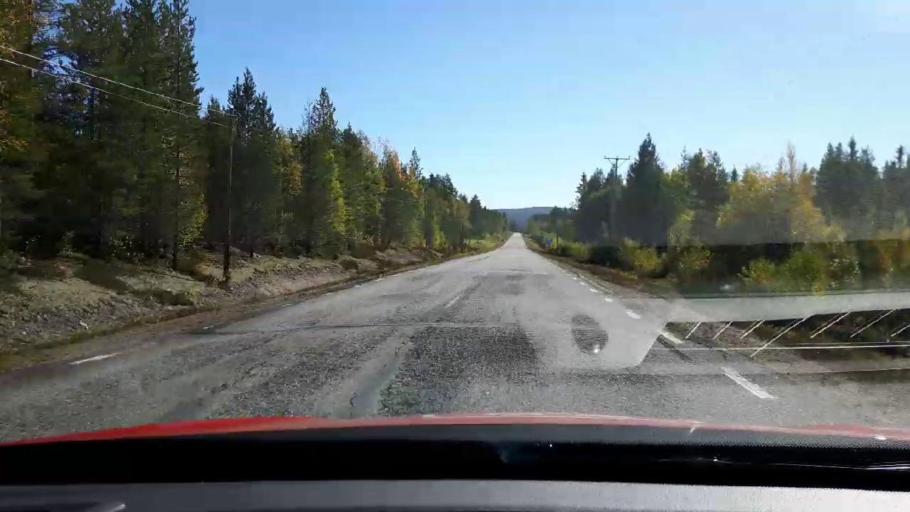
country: SE
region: Jaemtland
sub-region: Harjedalens Kommun
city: Sveg
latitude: 62.3021
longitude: 14.0602
